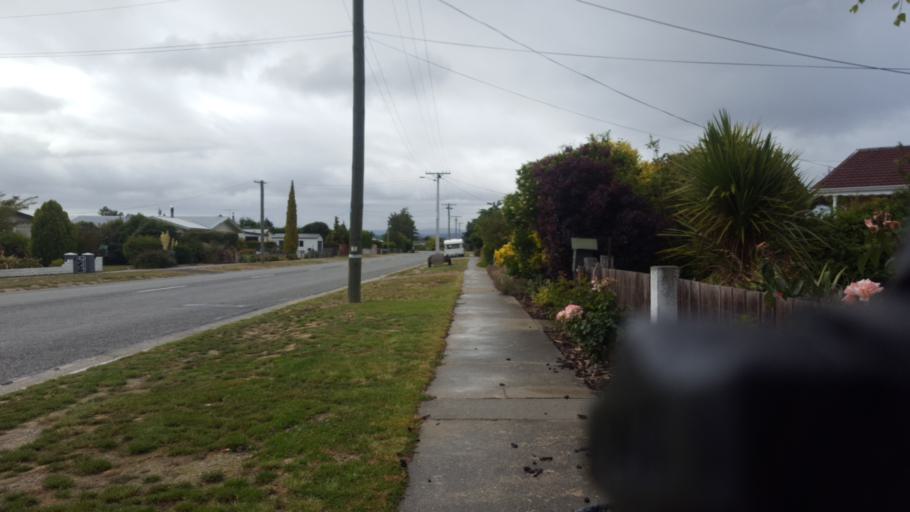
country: NZ
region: Otago
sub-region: Queenstown-Lakes District
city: Wanaka
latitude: -45.1910
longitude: 169.3280
